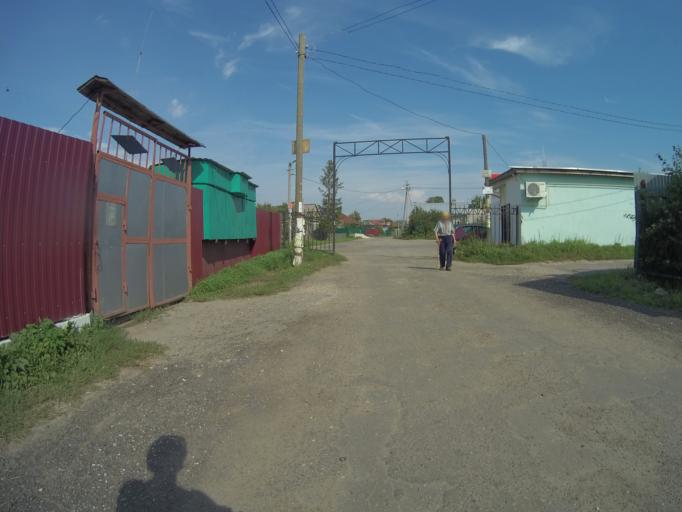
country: RU
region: Vladimir
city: Bogolyubovo
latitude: 56.1101
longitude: 40.5339
